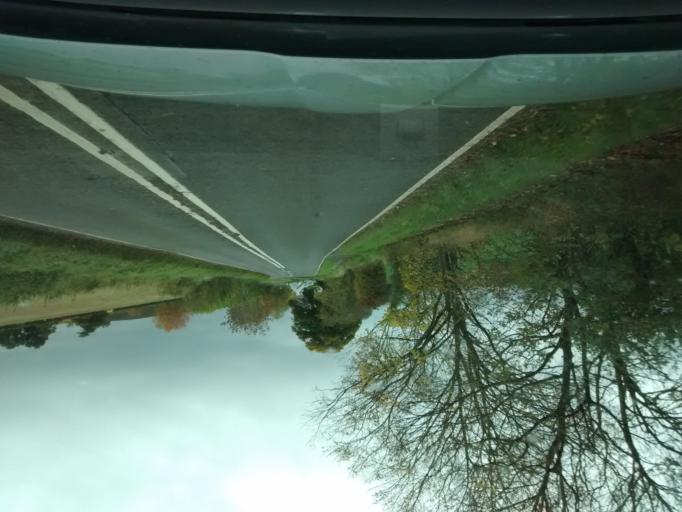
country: GB
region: Scotland
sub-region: Perth and Kinross
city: Auchterarder
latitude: 56.3041
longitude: -3.6797
